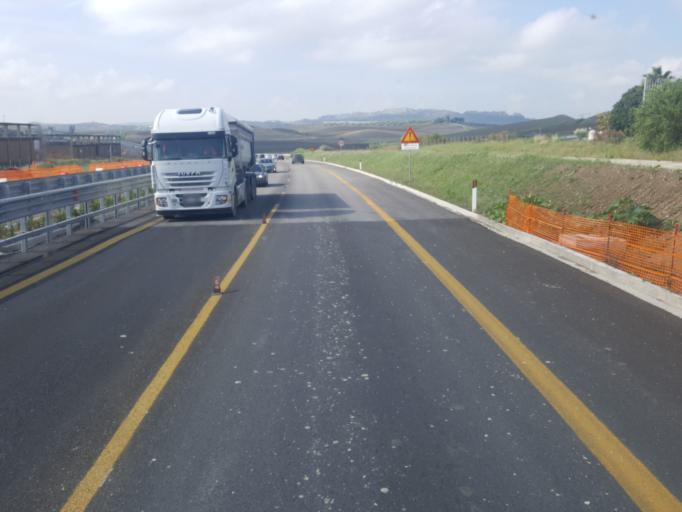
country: IT
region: Sicily
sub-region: Provincia di Caltanissetta
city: San Cataldo
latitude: 37.4463
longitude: 13.9557
